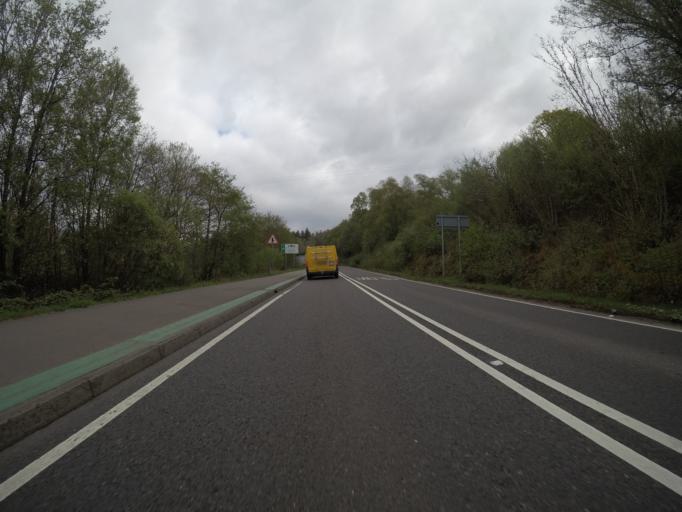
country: GB
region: Scotland
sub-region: Highland
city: Fort William
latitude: 56.7189
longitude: -5.2321
